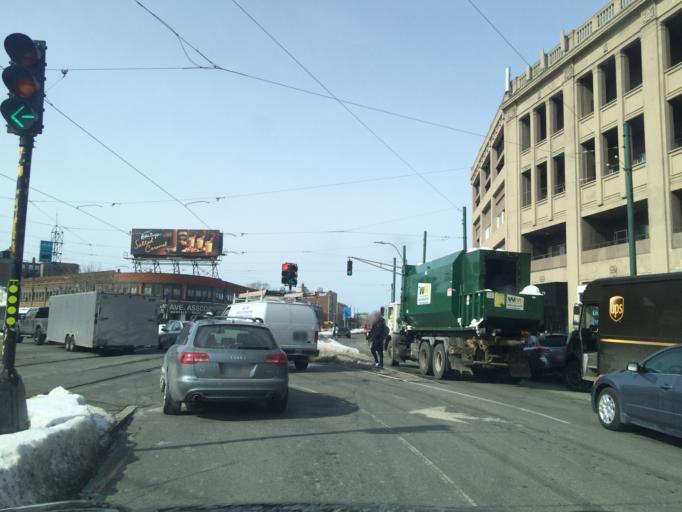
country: US
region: Massachusetts
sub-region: Norfolk County
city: Brookline
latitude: 42.3522
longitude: -71.1242
